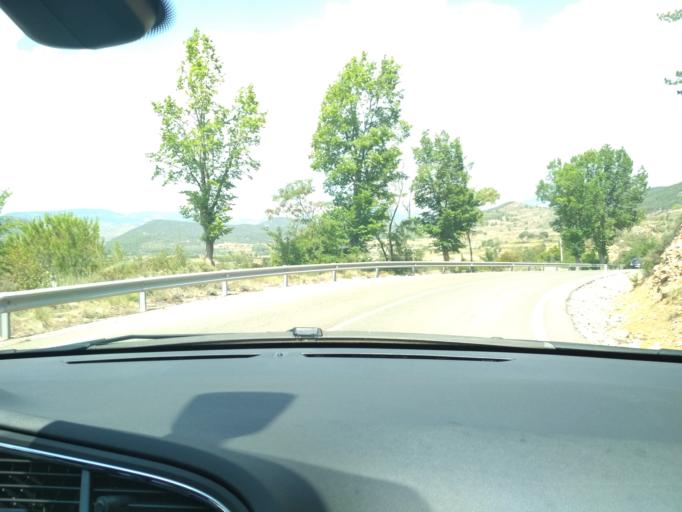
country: ES
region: Aragon
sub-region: Provincia de Teruel
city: Rubielos de Mora
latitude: 40.1892
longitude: -0.6487
